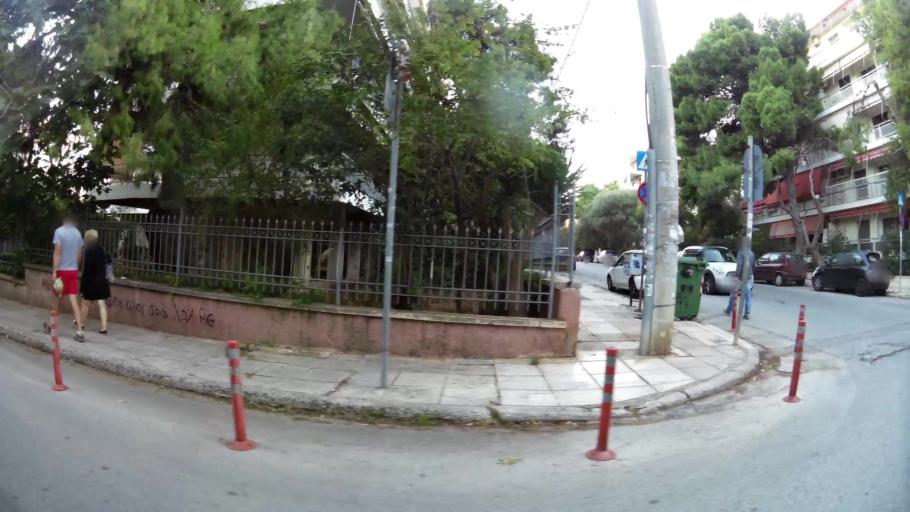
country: GR
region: Attica
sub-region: Nomarchia Anatolikis Attikis
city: Vari
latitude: 37.8203
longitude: 23.7986
